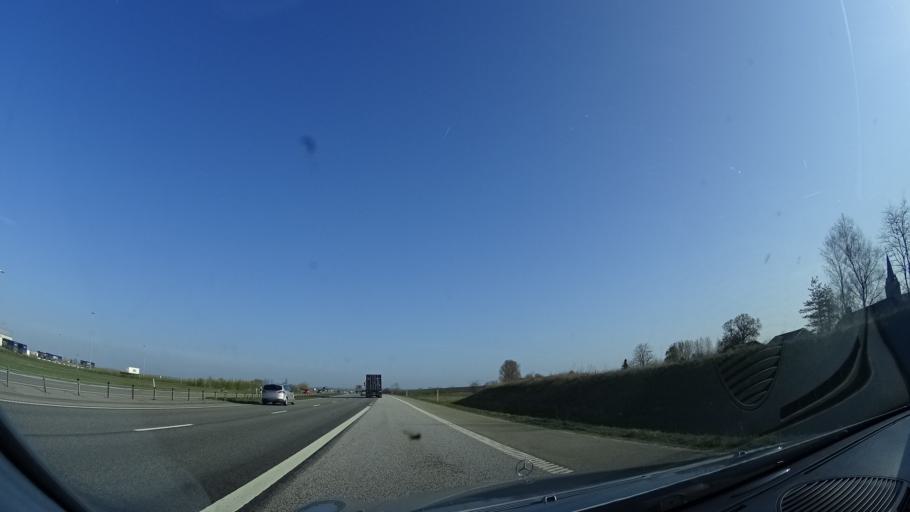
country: SE
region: Skane
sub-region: Landskrona
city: Landskrona
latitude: 55.8799
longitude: 12.8782
